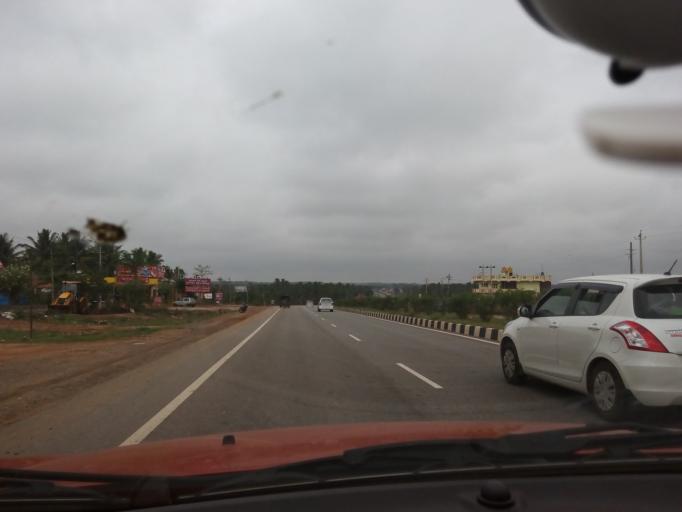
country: IN
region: Karnataka
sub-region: Hassan
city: Shravanabelagola
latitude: 12.9519
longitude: 76.5657
